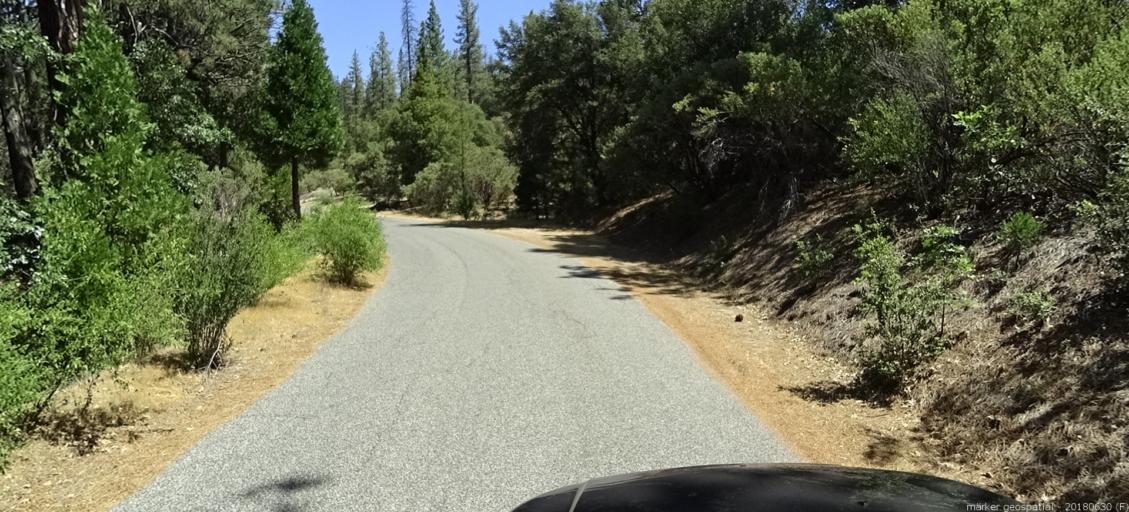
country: US
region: California
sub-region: Madera County
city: Oakhurst
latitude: 37.3572
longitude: -119.3445
